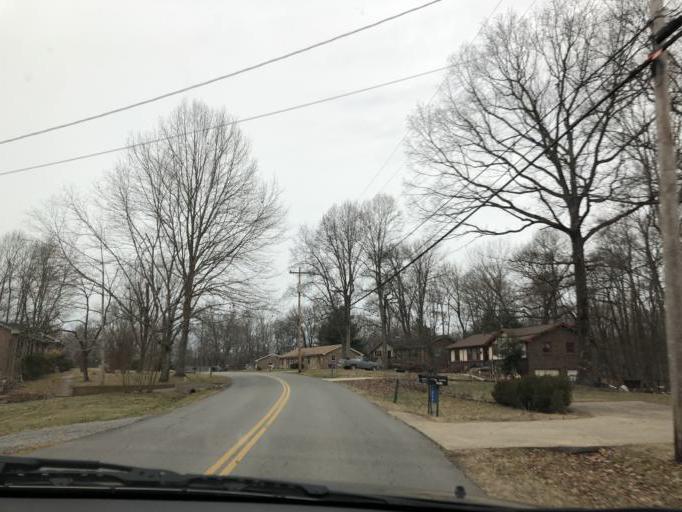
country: US
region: Tennessee
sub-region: Sumner County
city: White House
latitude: 36.4258
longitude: -86.6843
